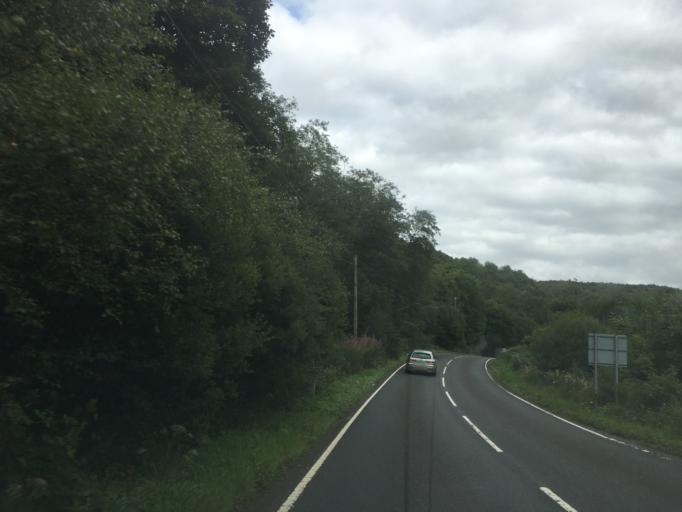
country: GB
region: Scotland
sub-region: Argyll and Bute
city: Oban
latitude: 56.3144
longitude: -5.4816
